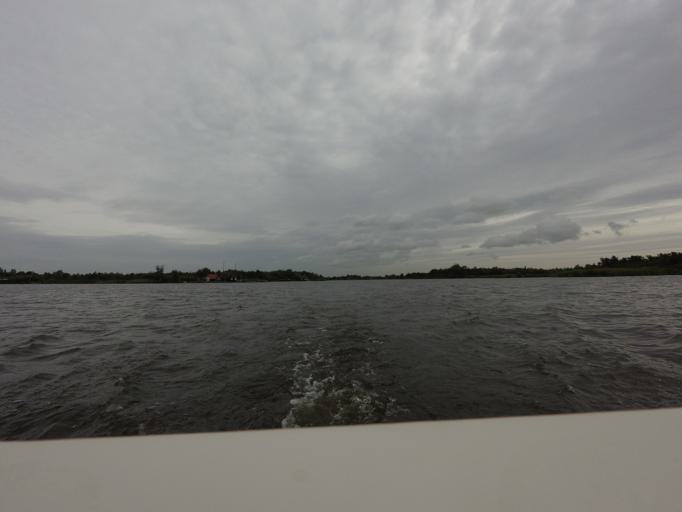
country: NL
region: Friesland
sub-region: Gemeente Boarnsterhim
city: Warten
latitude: 53.1231
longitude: 5.9160
